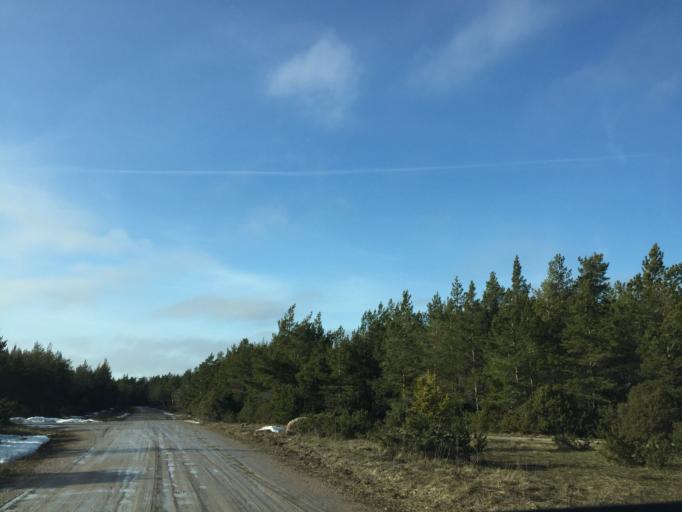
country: EE
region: Saare
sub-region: Kuressaare linn
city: Kuressaare
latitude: 58.4684
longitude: 21.9991
